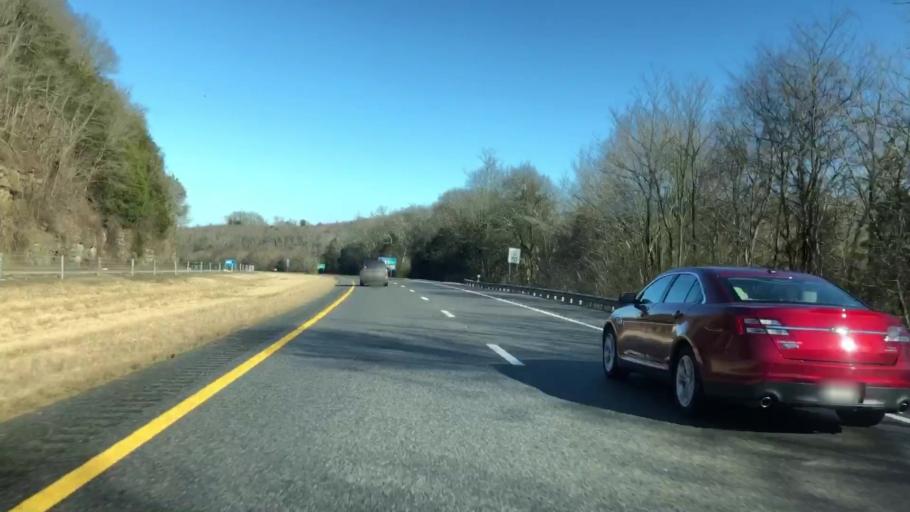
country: US
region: Alabama
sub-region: Limestone County
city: Ardmore
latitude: 34.9972
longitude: -86.8776
